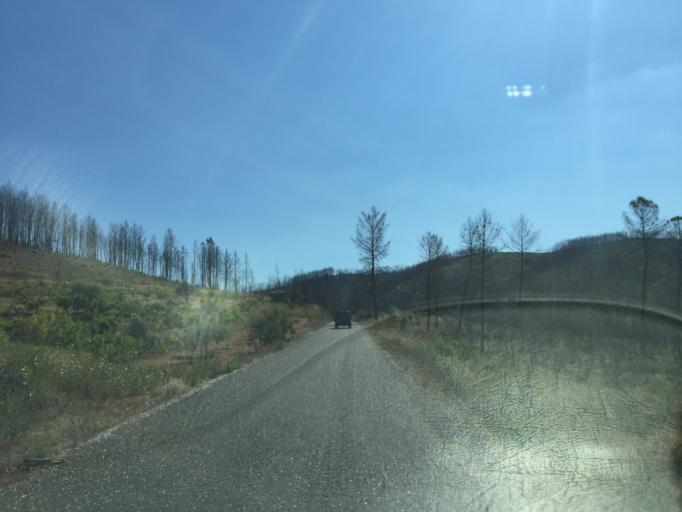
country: PT
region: Coimbra
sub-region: Pampilhosa da Serra
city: Pampilhosa da Serra
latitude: 40.0224
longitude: -7.8391
